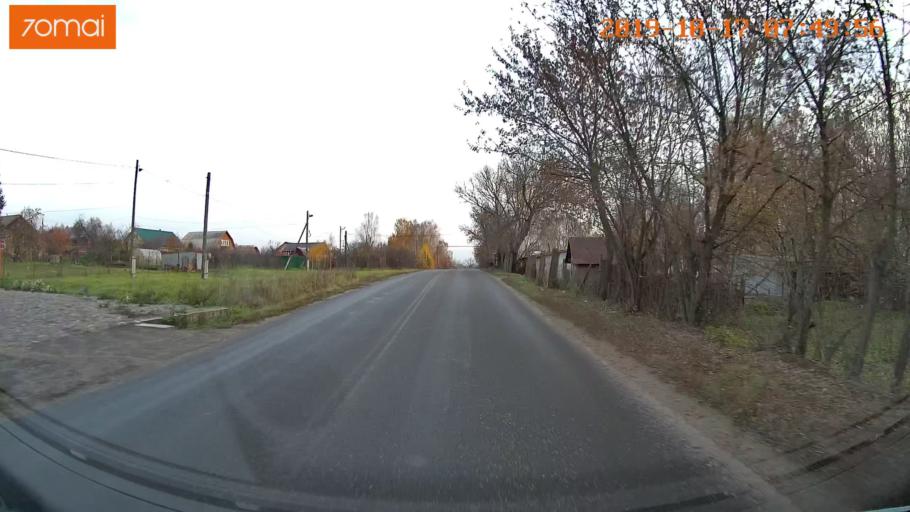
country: RU
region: Vladimir
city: Yur'yev-Pol'skiy
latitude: 56.4812
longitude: 39.6658
